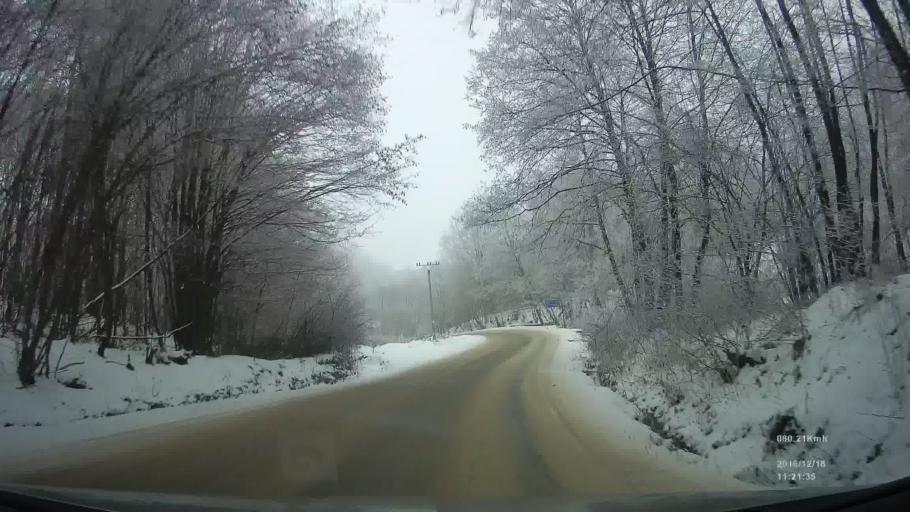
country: SK
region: Presovsky
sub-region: Okres Presov
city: Presov
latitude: 48.9065
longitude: 21.3722
